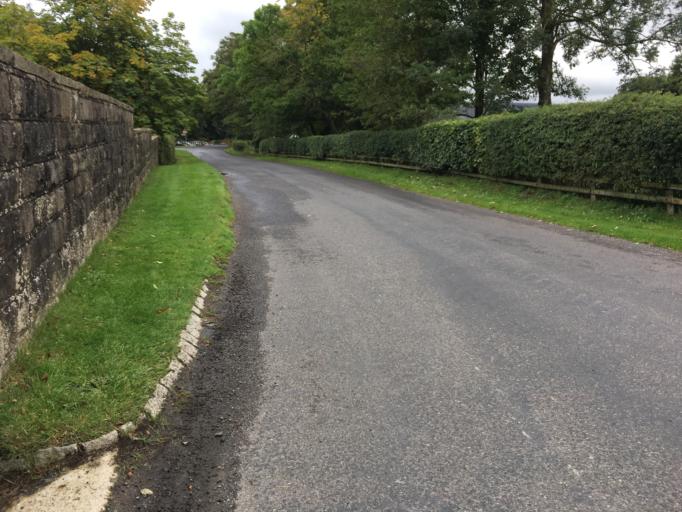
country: GB
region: England
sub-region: North Yorkshire
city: Danby
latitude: 54.4658
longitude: -0.8955
